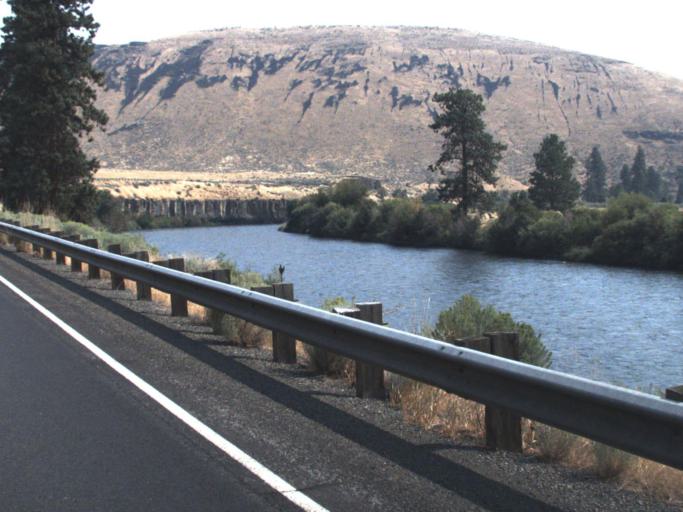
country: US
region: Washington
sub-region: Kittitas County
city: Kittitas
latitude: 46.8543
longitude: -120.4680
